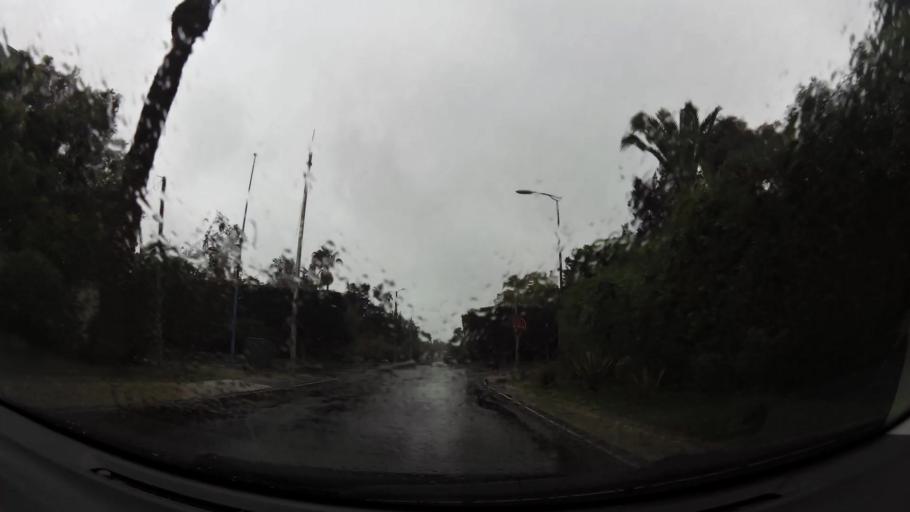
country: MA
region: Grand Casablanca
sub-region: Casablanca
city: Casablanca
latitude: 33.5851
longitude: -7.6661
